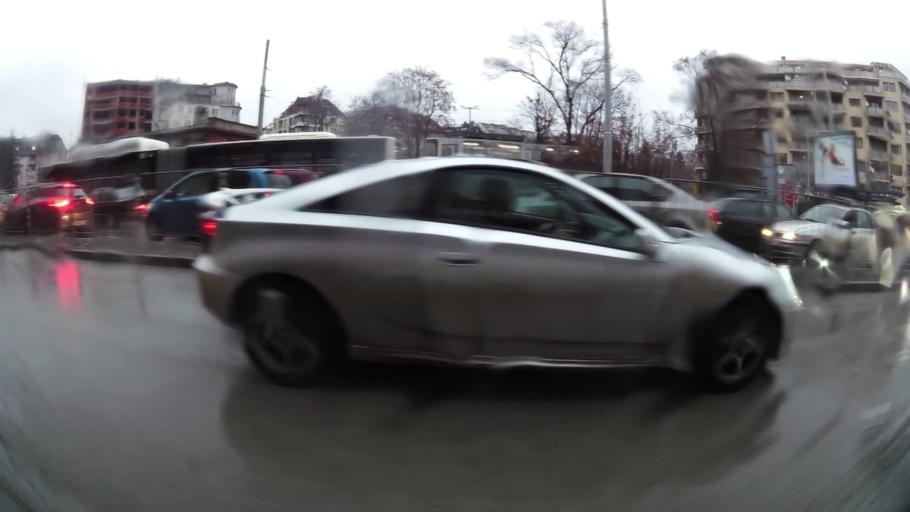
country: BG
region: Sofia-Capital
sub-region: Stolichna Obshtina
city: Sofia
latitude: 42.6599
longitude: 23.3177
